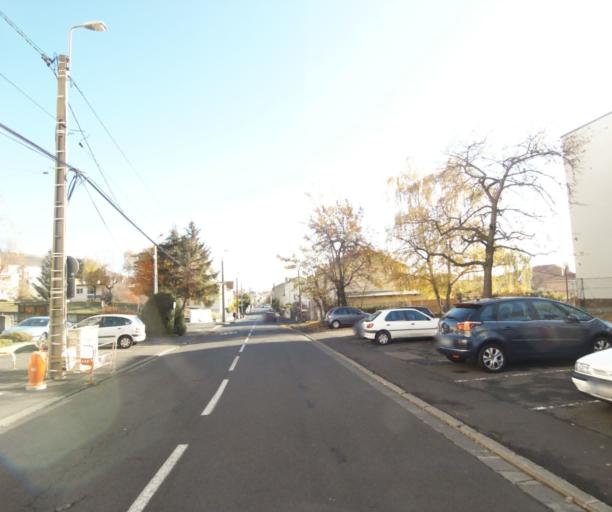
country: FR
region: Auvergne
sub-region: Departement du Puy-de-Dome
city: Clermont-Ferrand
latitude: 45.7935
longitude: 3.0769
